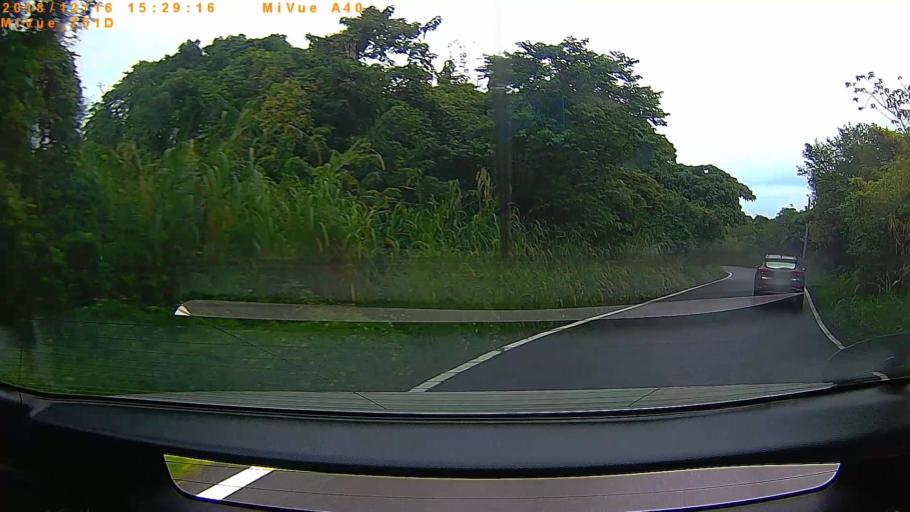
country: TW
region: Taiwan
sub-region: Hualien
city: Hualian
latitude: 23.9154
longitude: 121.6010
